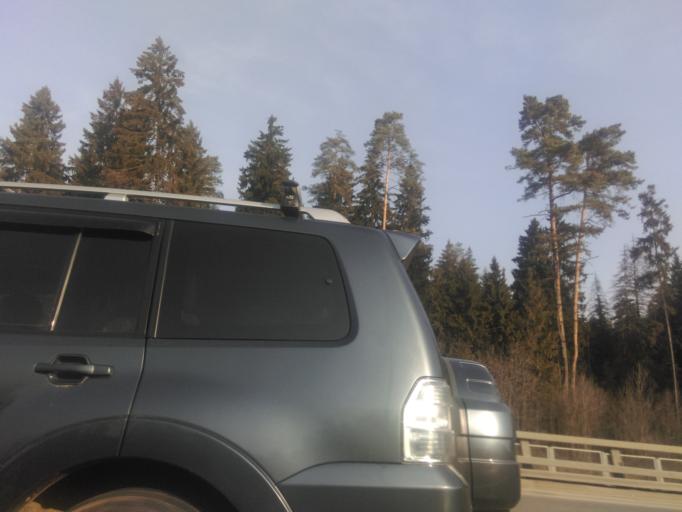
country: RU
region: Moskovskaya
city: Krasnoznamensk
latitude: 55.6101
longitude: 37.0616
